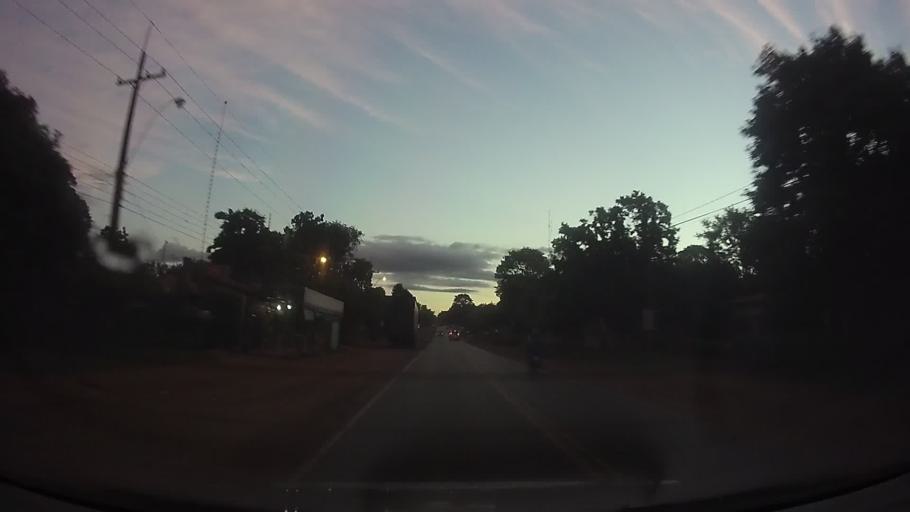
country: PY
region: Central
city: Ita
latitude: -25.4367
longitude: -57.3673
